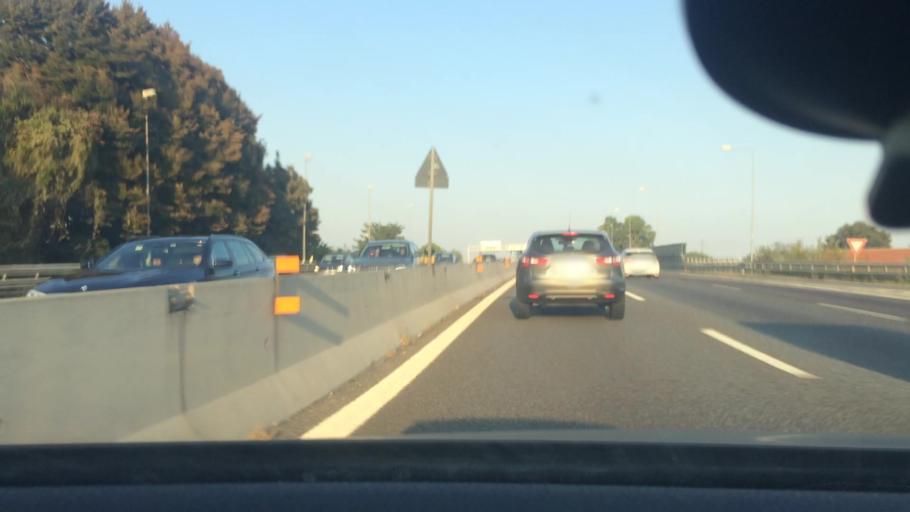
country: IT
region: Lombardy
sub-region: Citta metropolitana di Milano
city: Sesto San Giovanni
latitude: 45.5526
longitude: 9.2471
